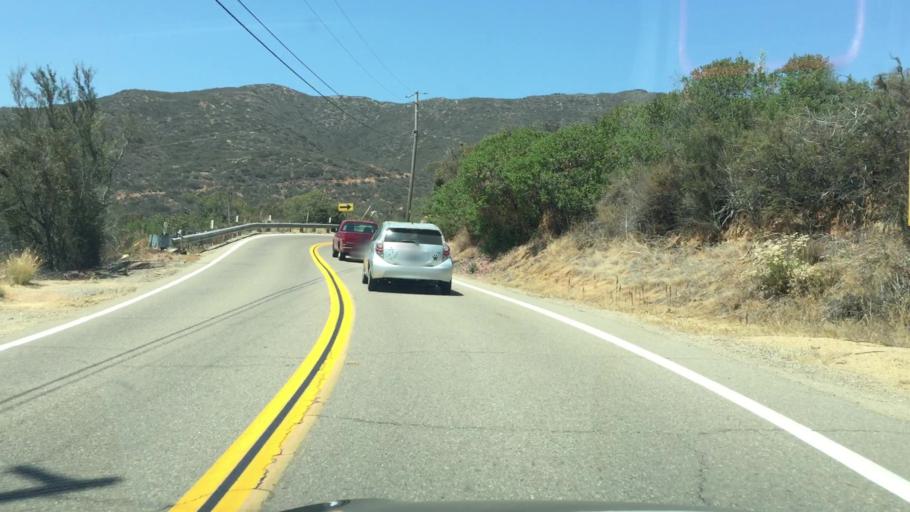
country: US
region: California
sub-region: San Diego County
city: Jamul
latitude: 32.7428
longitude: -116.8124
